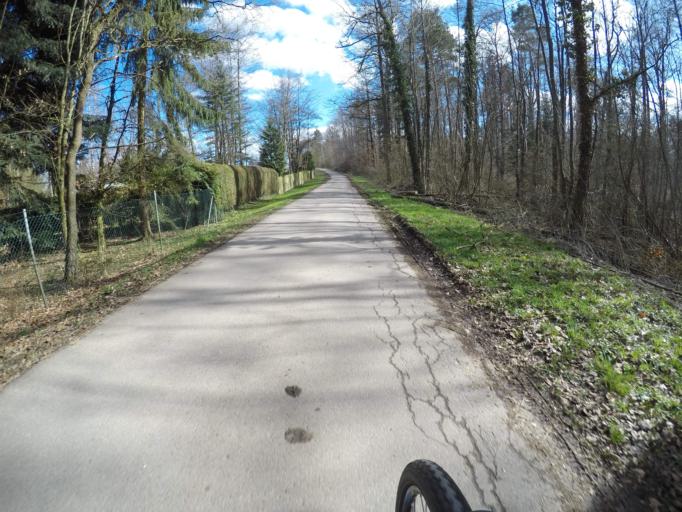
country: DE
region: Baden-Wuerttemberg
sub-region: Regierungsbezirk Stuttgart
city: Leinfelden-Echterdingen
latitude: 48.6780
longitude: 9.1539
